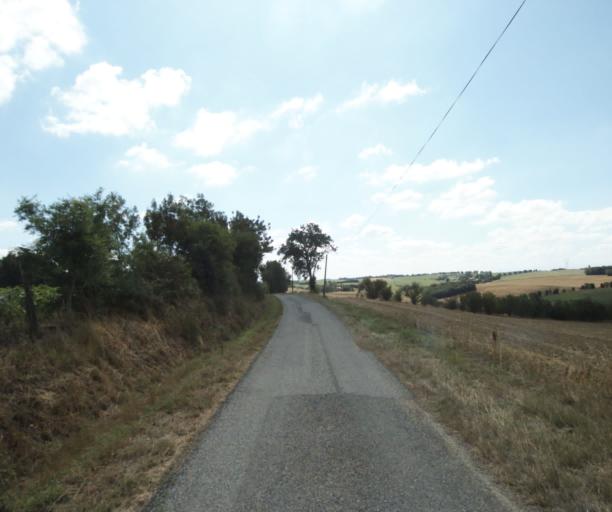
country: FR
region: Midi-Pyrenees
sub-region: Departement de la Haute-Garonne
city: Auriac-sur-Vendinelle
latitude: 43.4780
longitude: 1.8183
